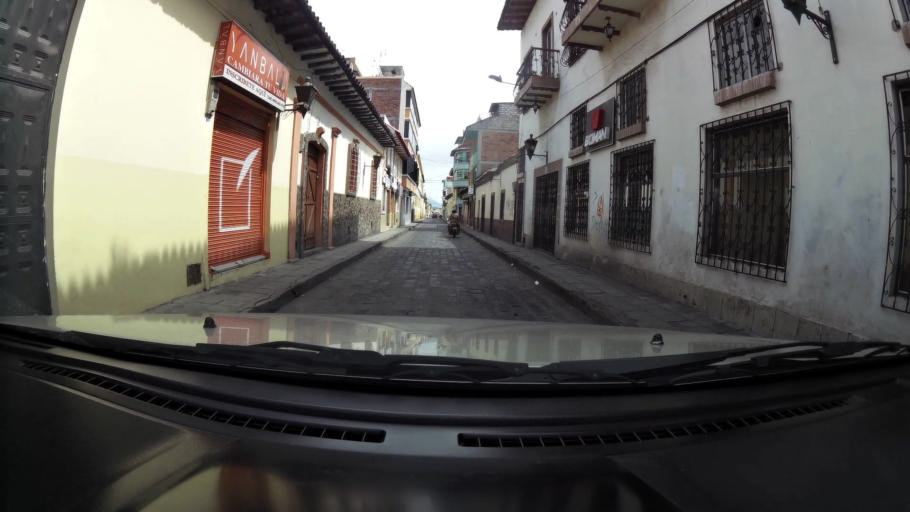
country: EC
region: Cotopaxi
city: Latacunga
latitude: -0.9294
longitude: -78.6077
